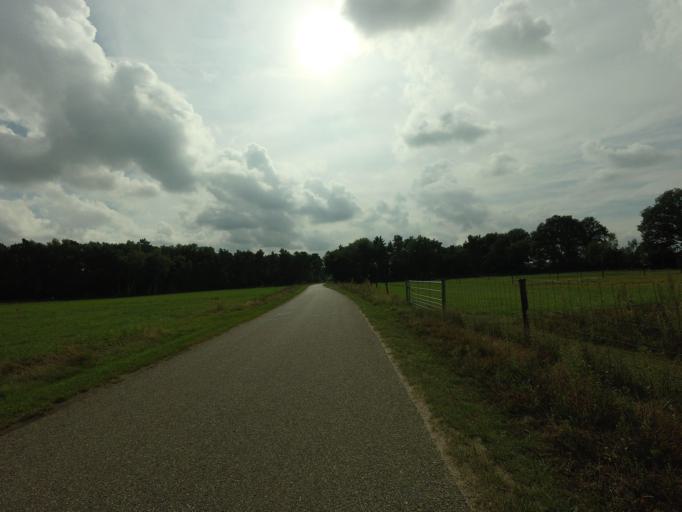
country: NL
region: Overijssel
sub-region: Gemeente Losser
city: Losser
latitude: 52.3172
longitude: 7.0305
